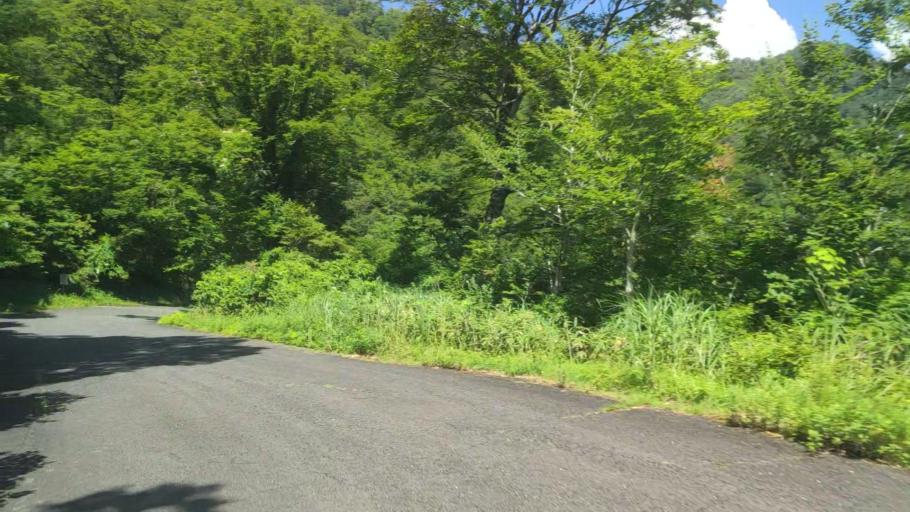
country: JP
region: Fukui
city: Ono
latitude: 35.7785
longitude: 136.5193
